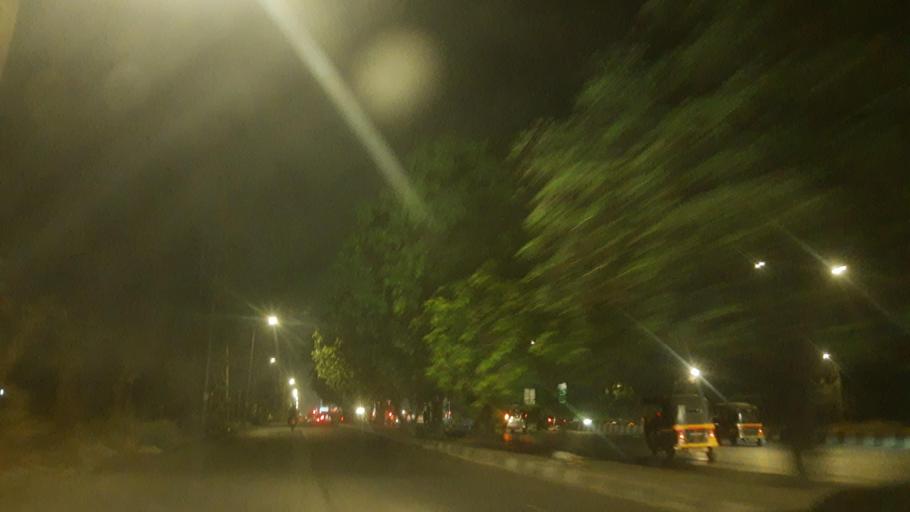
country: IN
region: Maharashtra
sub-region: Thane
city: Airoli
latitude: 19.1586
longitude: 72.9600
